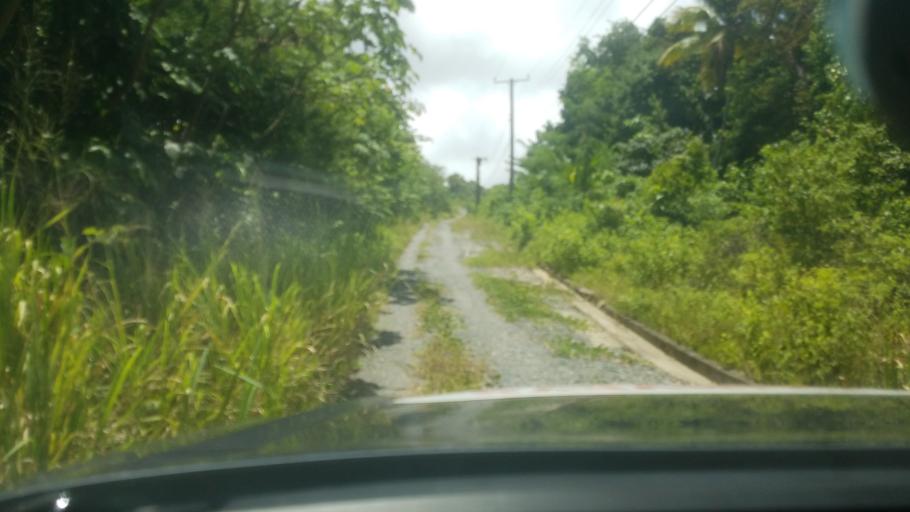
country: LC
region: Praslin
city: Praslin
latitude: 13.8719
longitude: -60.9126
